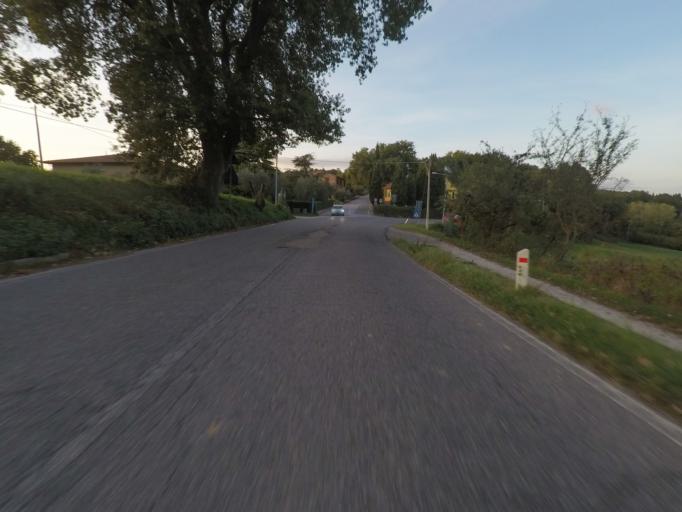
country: IT
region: Tuscany
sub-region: Provincia di Siena
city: Torrita di Siena
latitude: 43.1338
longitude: 11.7296
